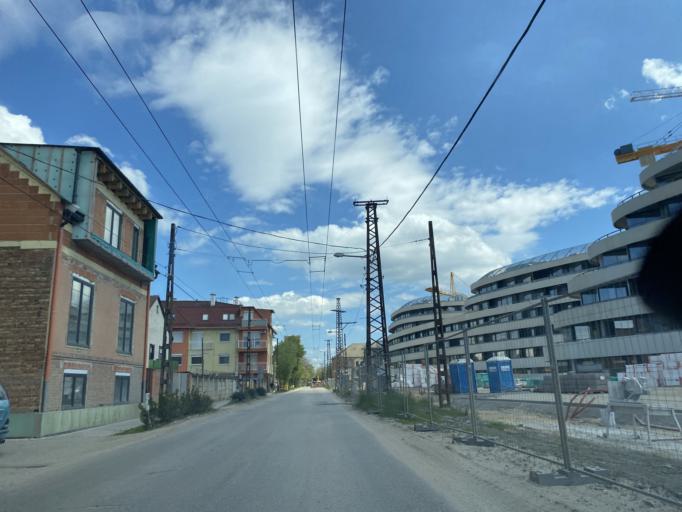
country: HU
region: Csongrad
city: Szeged
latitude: 46.2576
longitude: 20.1314
